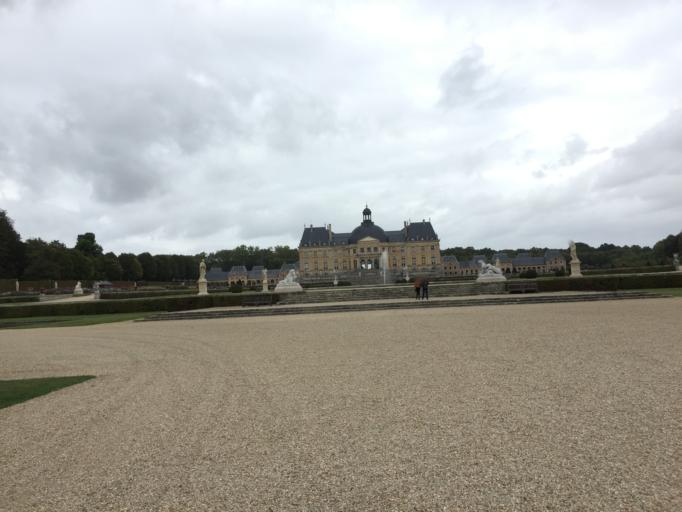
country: FR
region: Ile-de-France
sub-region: Departement de Seine-et-Marne
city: Maincy
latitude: 48.5632
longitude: 2.7146
